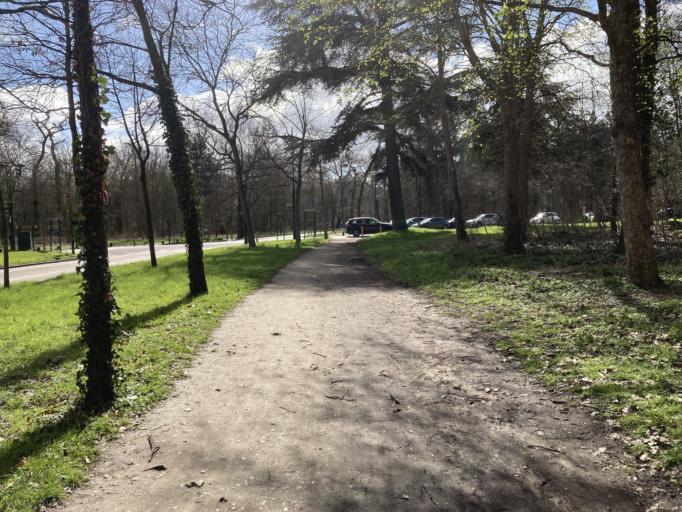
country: FR
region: Ile-de-France
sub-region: Departement des Hauts-de-Seine
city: Neuilly-sur-Seine
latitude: 48.8730
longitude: 2.2642
